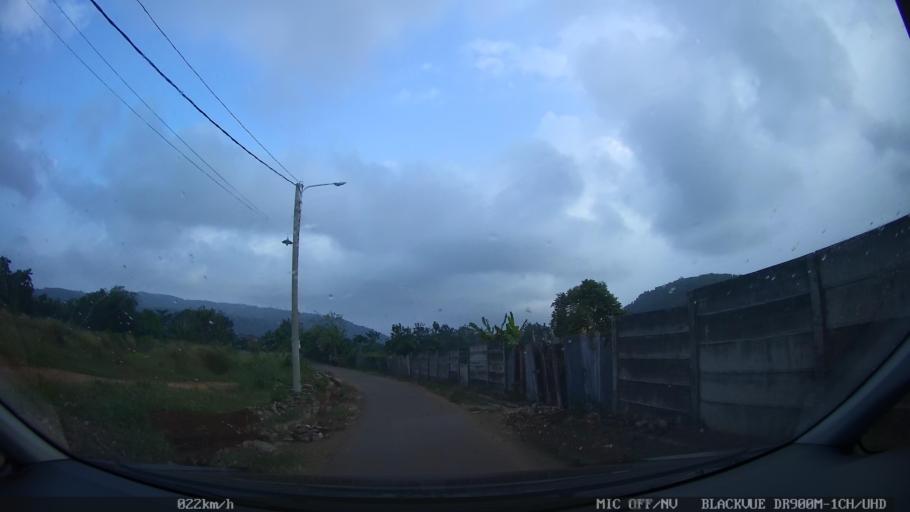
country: ID
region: Lampung
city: Bandarlampung
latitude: -5.4165
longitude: 105.2873
